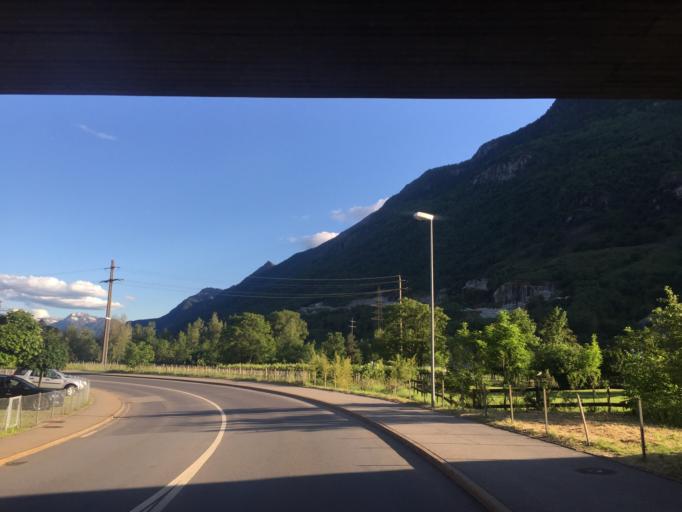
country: CH
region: Ticino
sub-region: Riviera District
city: Biasca
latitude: 46.3601
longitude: 8.9557
